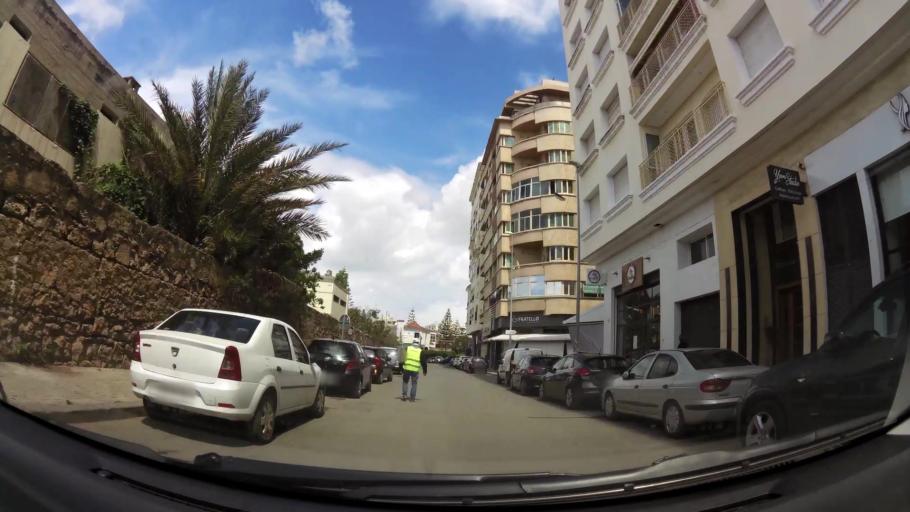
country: MA
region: Grand Casablanca
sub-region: Casablanca
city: Casablanca
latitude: 33.5760
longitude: -7.6477
